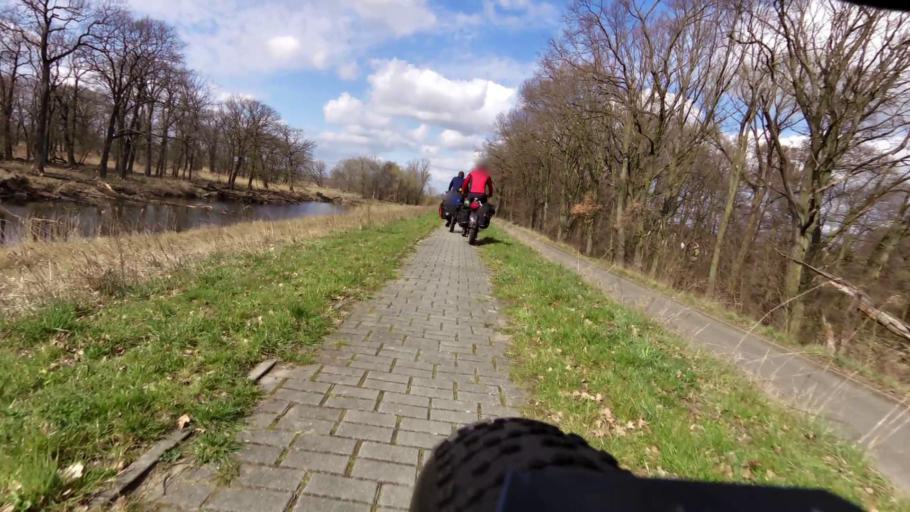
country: PL
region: Lubusz
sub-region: Powiat slubicki
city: Slubice
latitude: 52.3736
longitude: 14.5598
